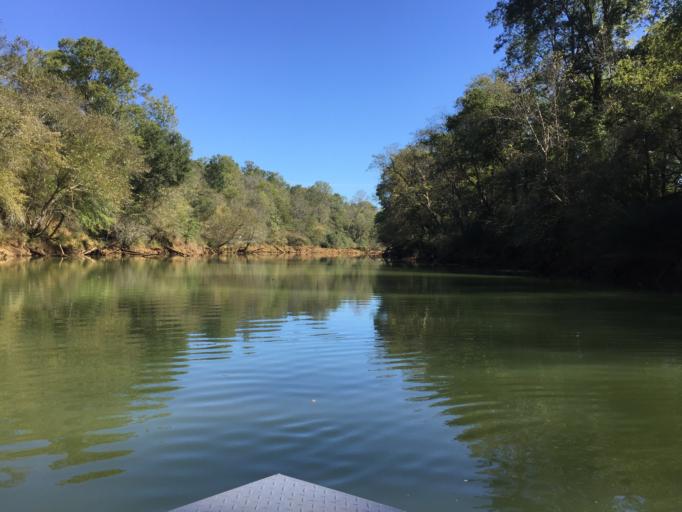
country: US
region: Georgia
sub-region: Gwinnett County
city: Suwanee
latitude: 34.0453
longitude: -84.1067
